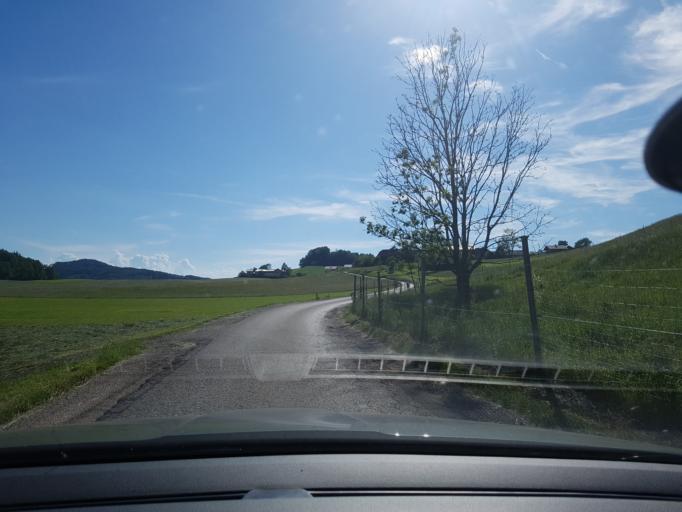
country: AT
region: Salzburg
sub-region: Politischer Bezirk Salzburg-Umgebung
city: Schleedorf
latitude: 47.9758
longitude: 13.1434
